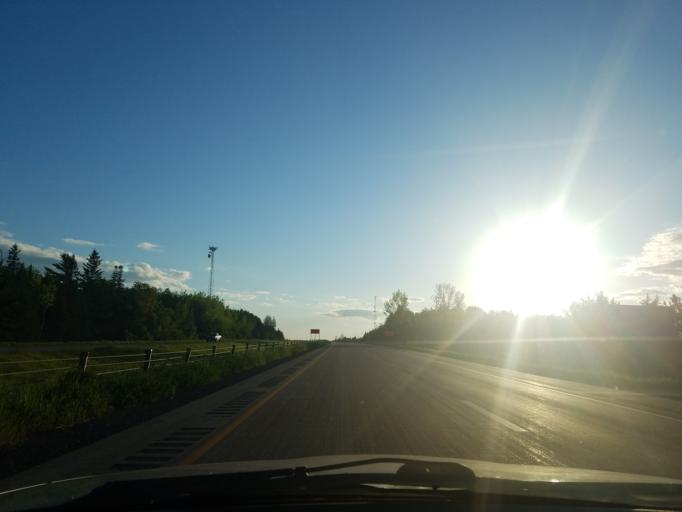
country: US
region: Minnesota
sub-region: Carlton County
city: Esko
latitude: 46.6994
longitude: -92.3928
